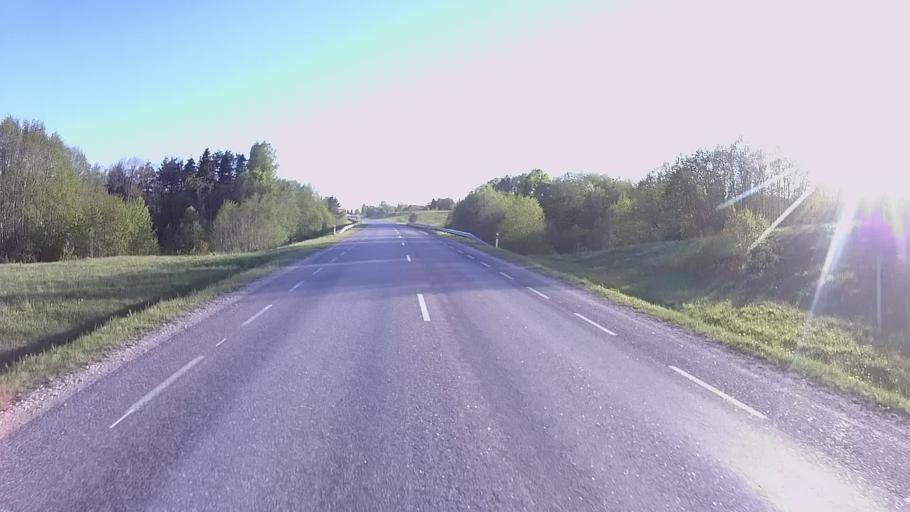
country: EE
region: Viljandimaa
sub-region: Viiratsi vald
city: Viiratsi
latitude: 58.4046
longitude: 25.6597
